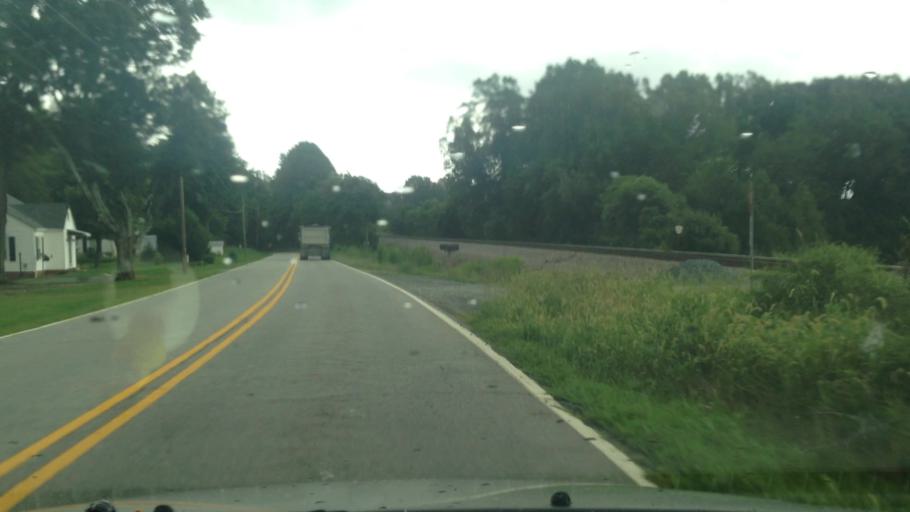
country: US
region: North Carolina
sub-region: Forsyth County
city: Walkertown
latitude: 36.1874
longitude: -80.1613
